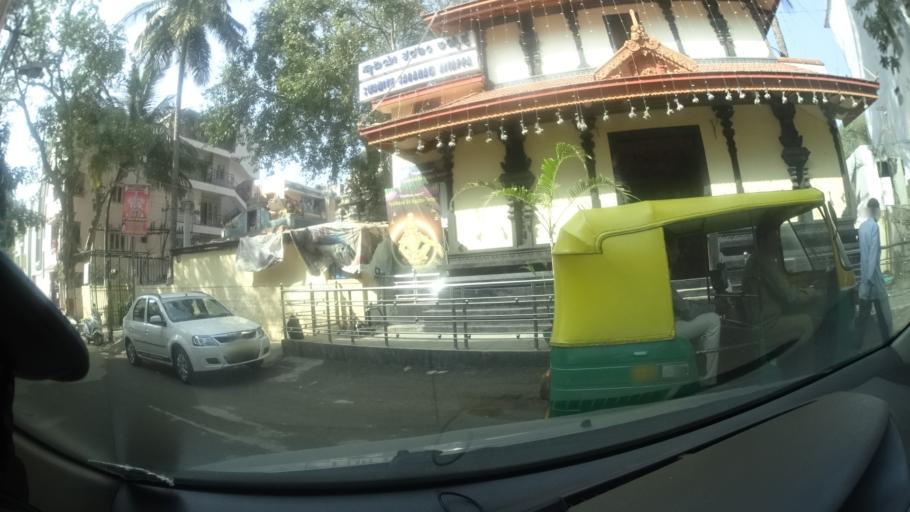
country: IN
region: Karnataka
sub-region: Bangalore Urban
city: Bangalore
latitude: 13.0044
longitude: 77.5755
